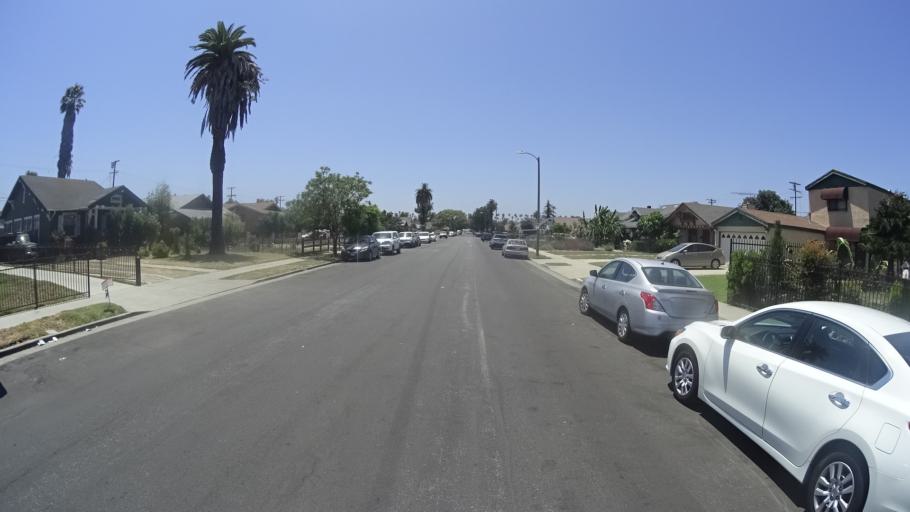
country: US
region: California
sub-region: Los Angeles County
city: View Park-Windsor Hills
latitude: 33.9979
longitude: -118.3099
